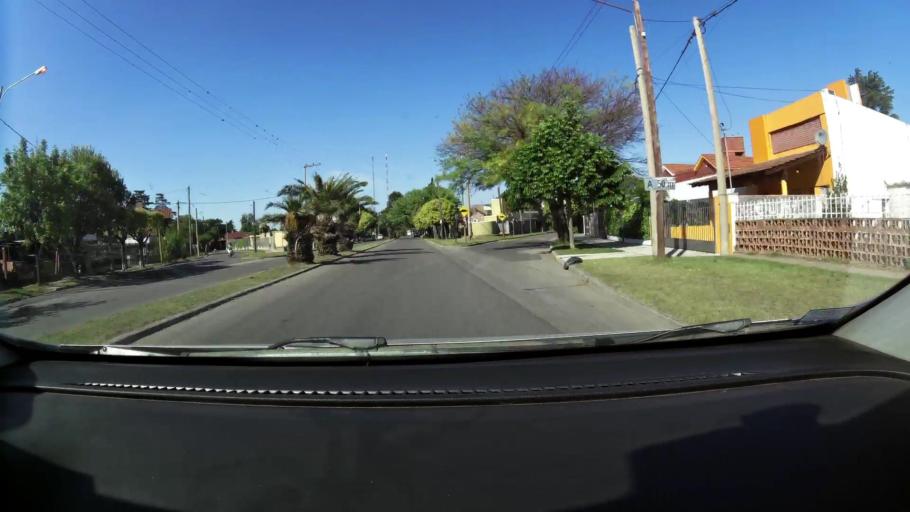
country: AR
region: Cordoba
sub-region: Departamento de Capital
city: Cordoba
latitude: -31.3611
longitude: -64.2021
